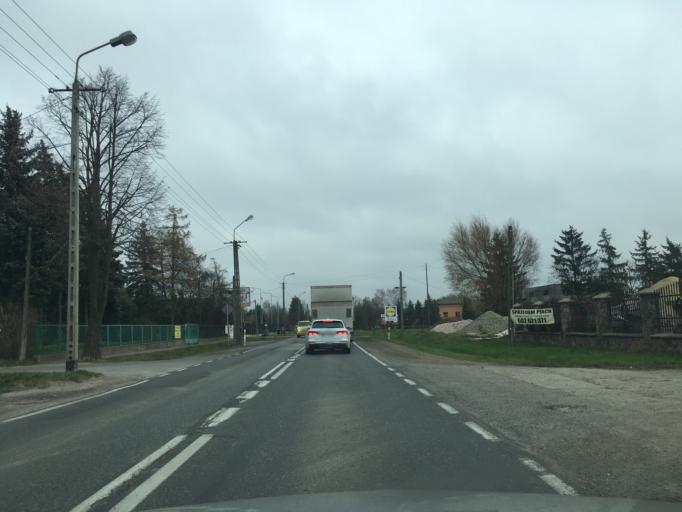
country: PL
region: Masovian Voivodeship
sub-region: Powiat piaseczynski
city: Piaseczno
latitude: 52.0816
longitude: 20.9870
